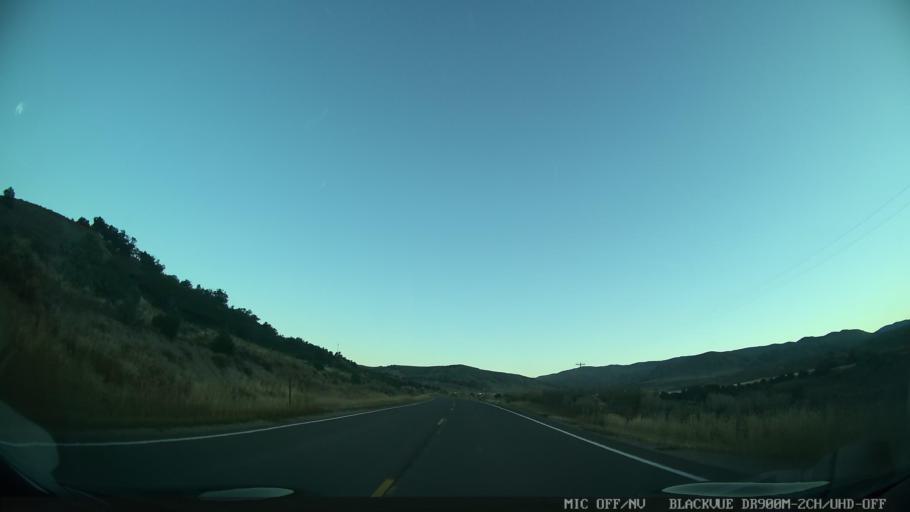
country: US
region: Colorado
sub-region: Eagle County
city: Edwards
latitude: 39.7312
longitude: -106.6788
